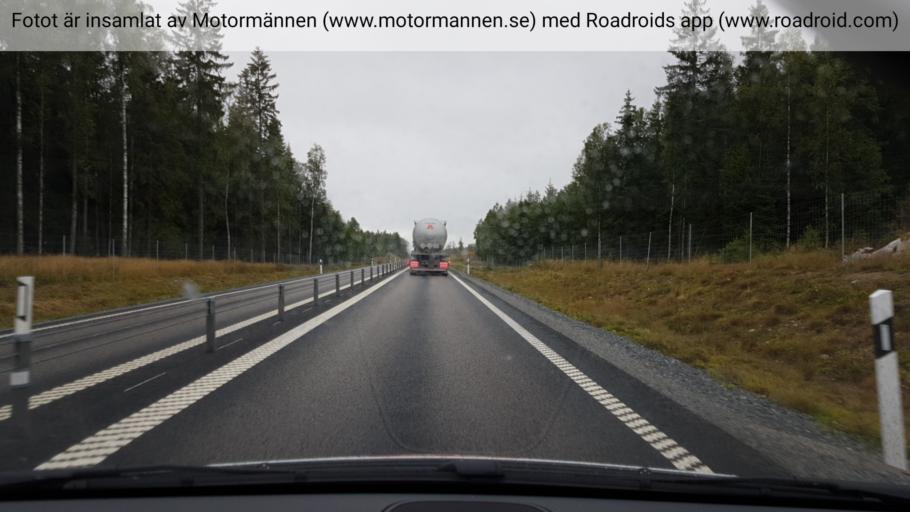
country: SE
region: Uppsala
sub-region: Heby Kommun
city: Heby
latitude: 59.9864
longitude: 16.8534
